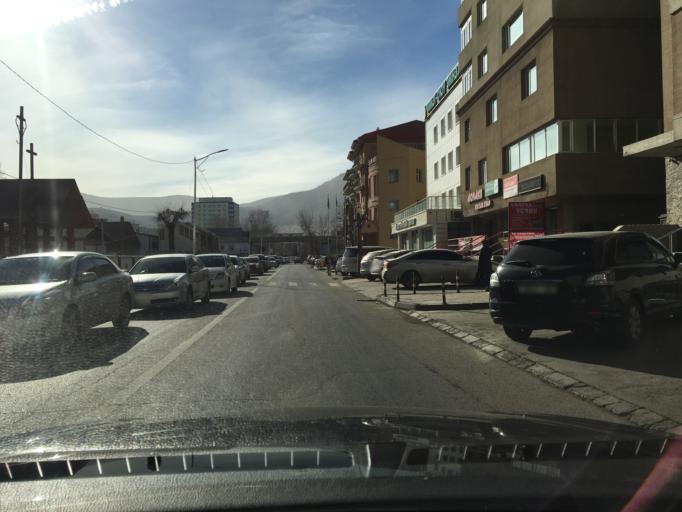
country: MN
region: Ulaanbaatar
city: Ulaanbaatar
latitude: 47.8971
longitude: 106.8962
